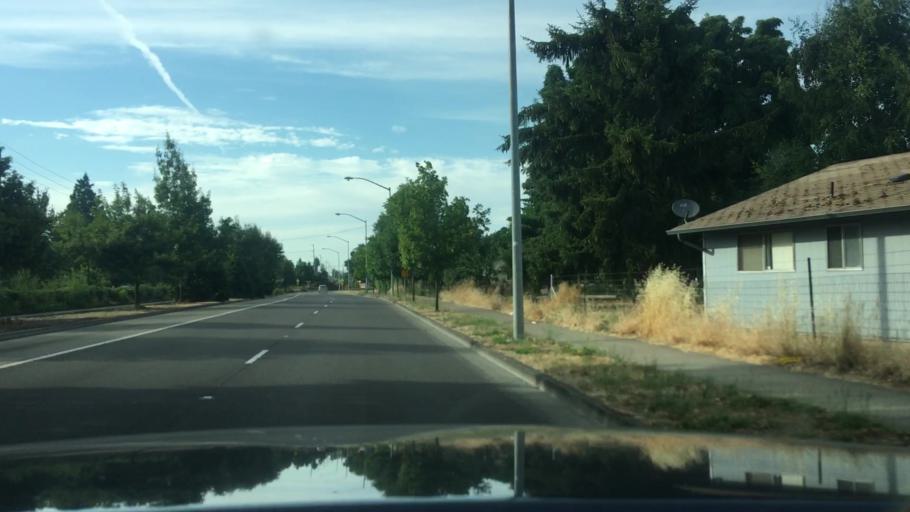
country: US
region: Oregon
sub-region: Lane County
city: Springfield
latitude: 44.0683
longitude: -123.0278
